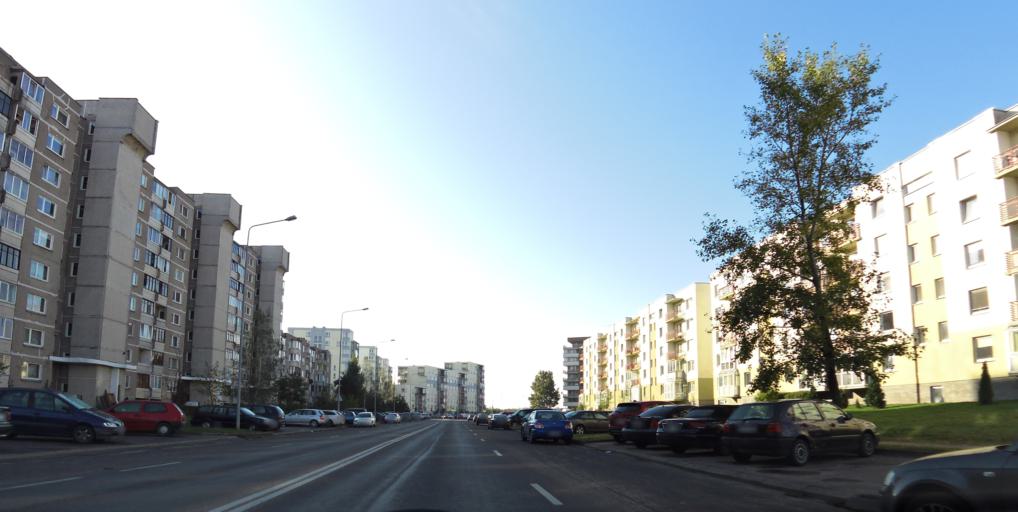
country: LT
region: Vilnius County
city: Pilaite
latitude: 54.7063
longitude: 25.1749
